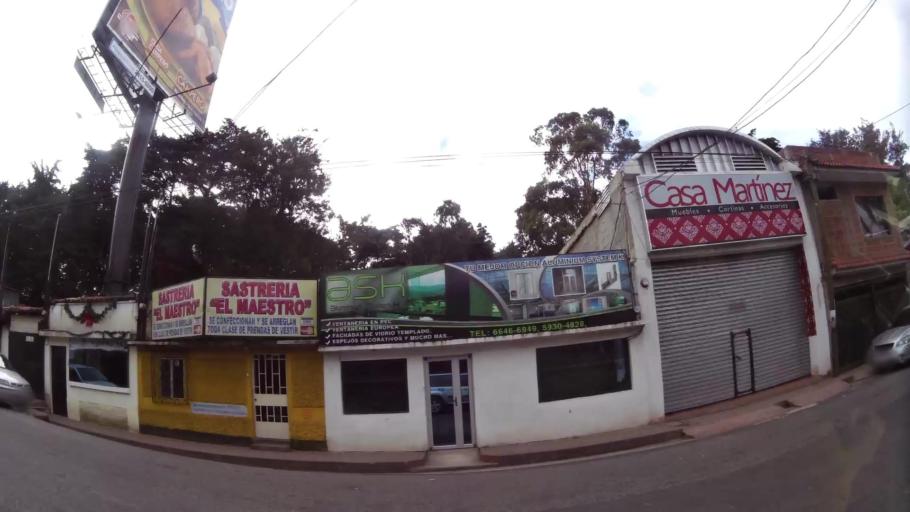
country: GT
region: Guatemala
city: Santa Catarina Pinula
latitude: 14.5647
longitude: -90.4687
